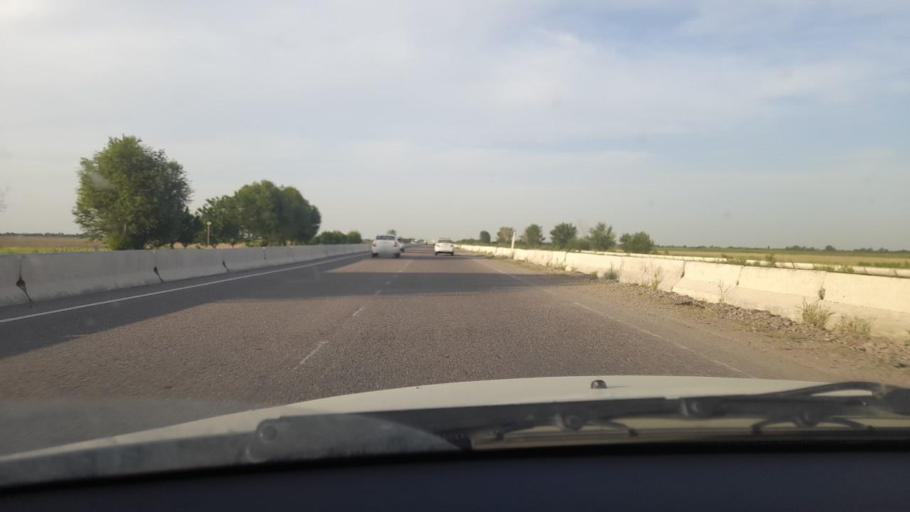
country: UZ
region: Jizzax
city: Gagarin
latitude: 40.4727
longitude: 68.2756
